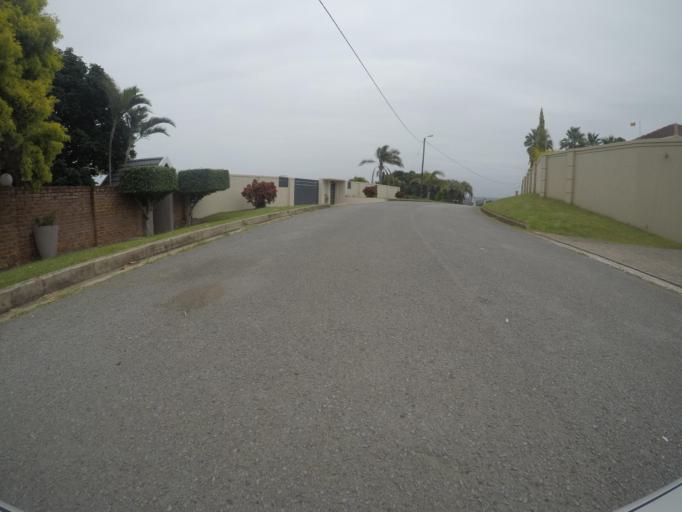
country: ZA
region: Eastern Cape
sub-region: Buffalo City Metropolitan Municipality
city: East London
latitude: -32.9781
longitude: 27.9367
